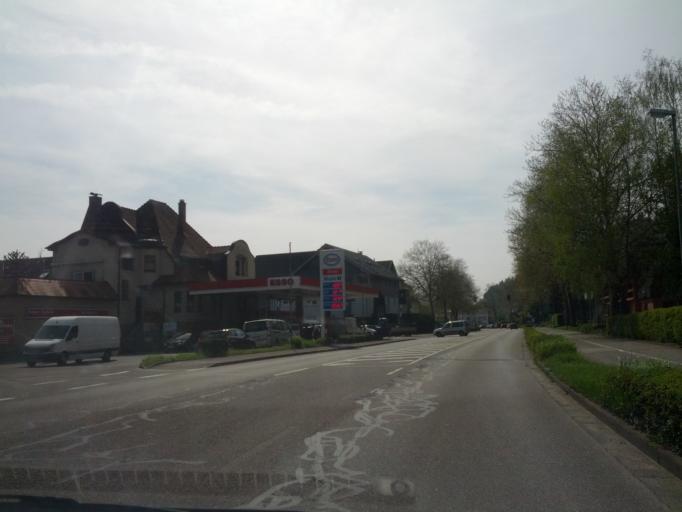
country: DE
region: Baden-Wuerttemberg
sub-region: Freiburg Region
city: Waldkirch
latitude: 48.0906
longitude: 7.9533
